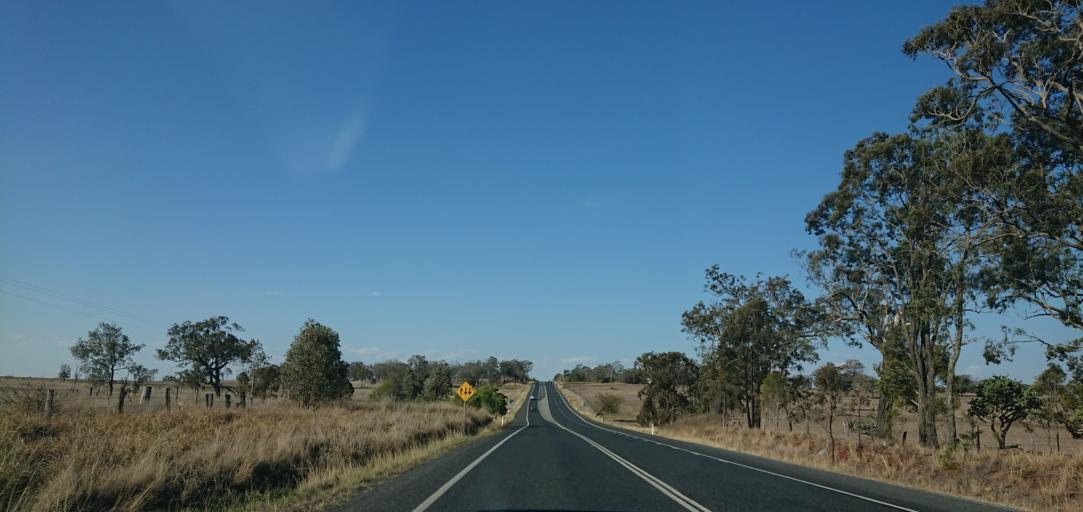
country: AU
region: Queensland
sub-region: Toowoomba
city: Westbrook
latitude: -27.6301
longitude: 151.7534
